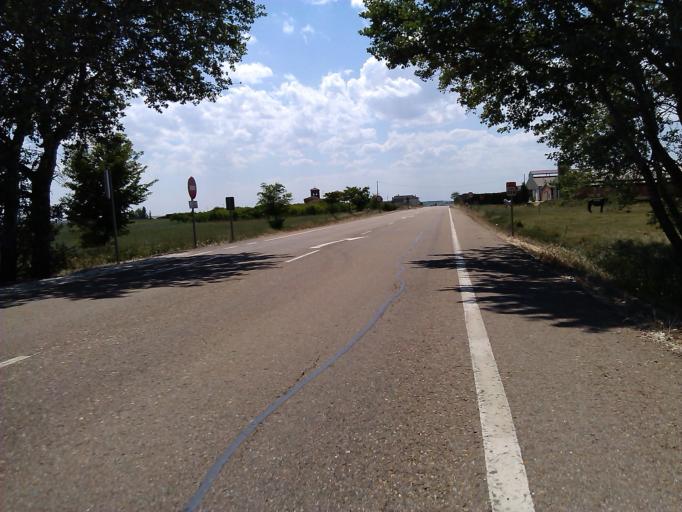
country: ES
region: Castille and Leon
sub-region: Provincia de Palencia
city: Ledigos
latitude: 42.3650
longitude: -4.8854
